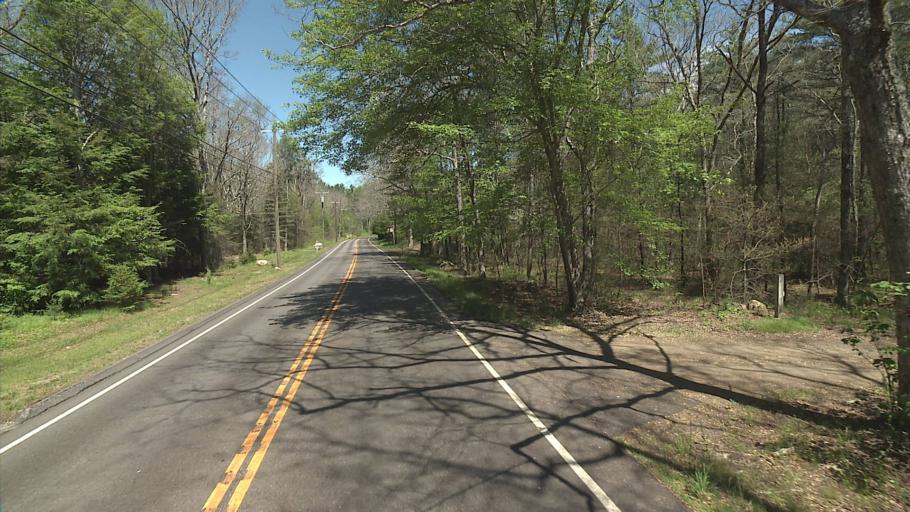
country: US
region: Connecticut
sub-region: Windham County
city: Plainfield
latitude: 41.5704
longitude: -71.8595
